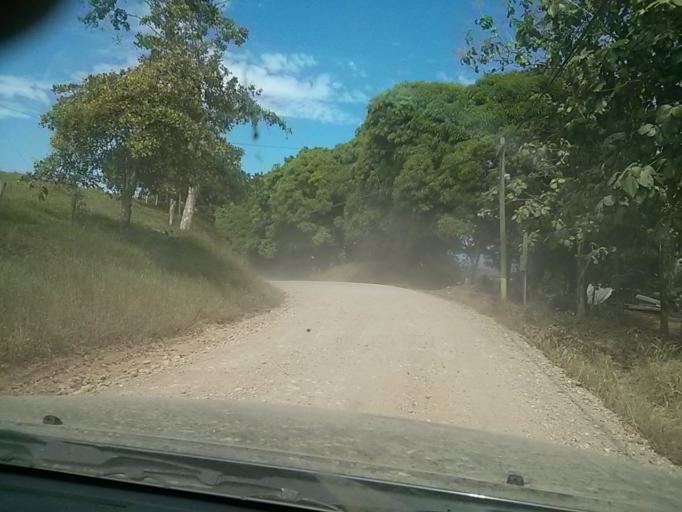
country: CR
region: Puntarenas
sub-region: Canton de Golfito
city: Golfito
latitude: 8.4511
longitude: -83.0566
